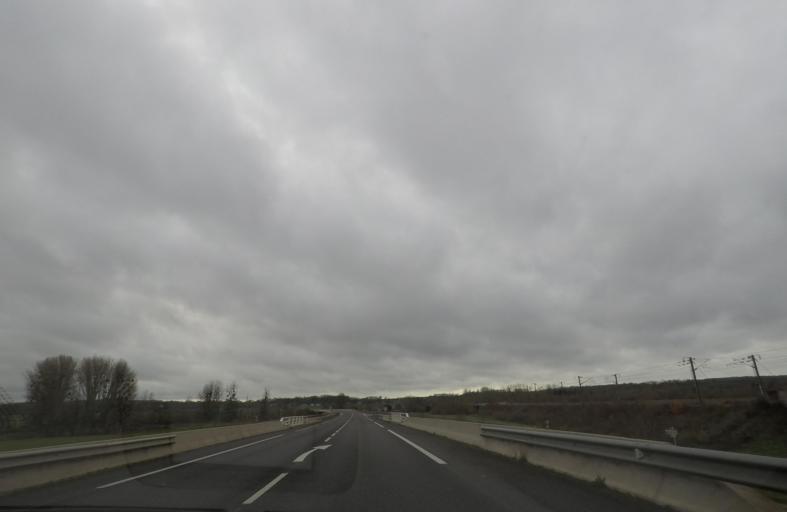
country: FR
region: Centre
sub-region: Departement du Loir-et-Cher
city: Villiers-sur-Loir
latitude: 47.7870
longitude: 1.0049
